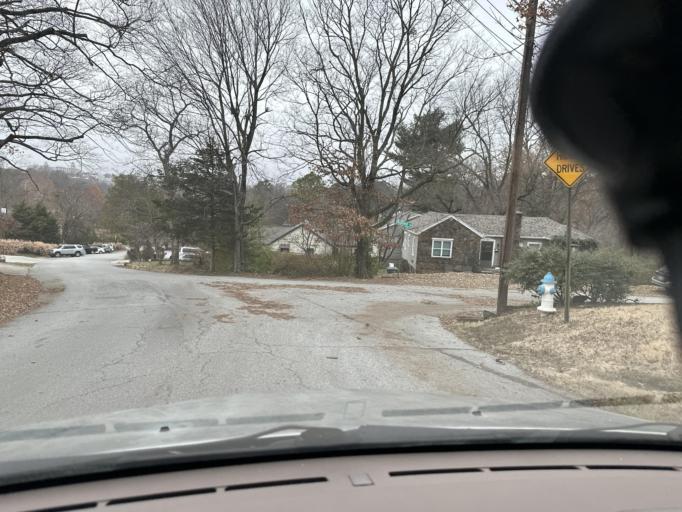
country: US
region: Arkansas
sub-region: Washington County
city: Fayetteville
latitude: 36.0738
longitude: -94.1590
